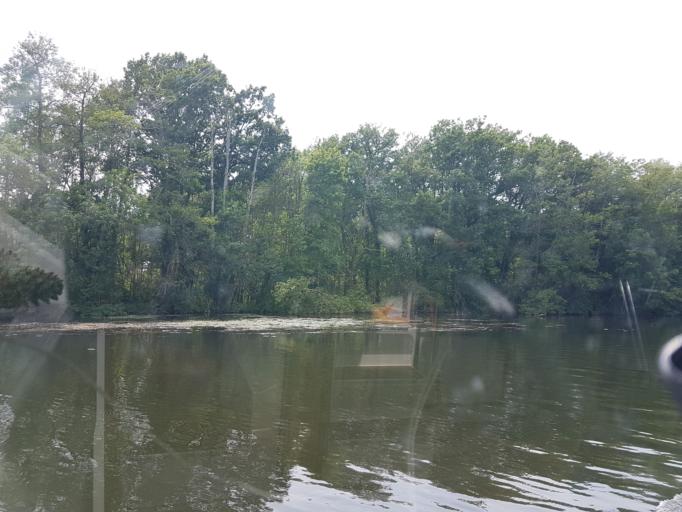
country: FR
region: Bourgogne
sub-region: Departement de l'Yonne
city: Gurgy
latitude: 47.8598
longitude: 3.5541
